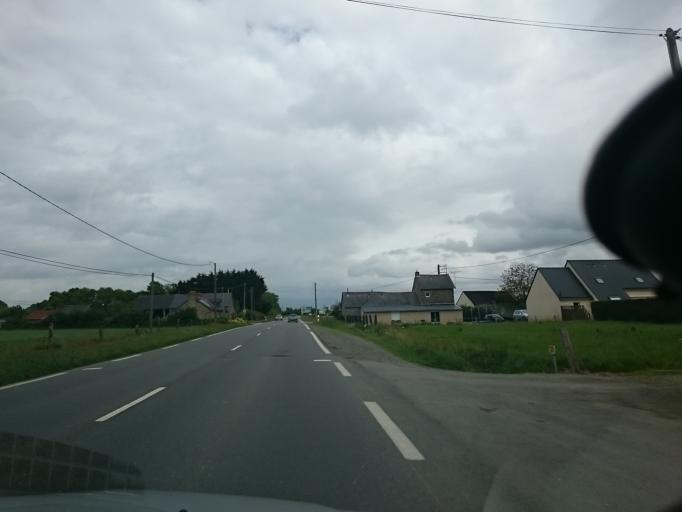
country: FR
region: Brittany
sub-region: Departement d'Ille-et-Vilaine
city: Saint-Brice-en-Cogles
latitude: 48.4187
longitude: -1.3950
